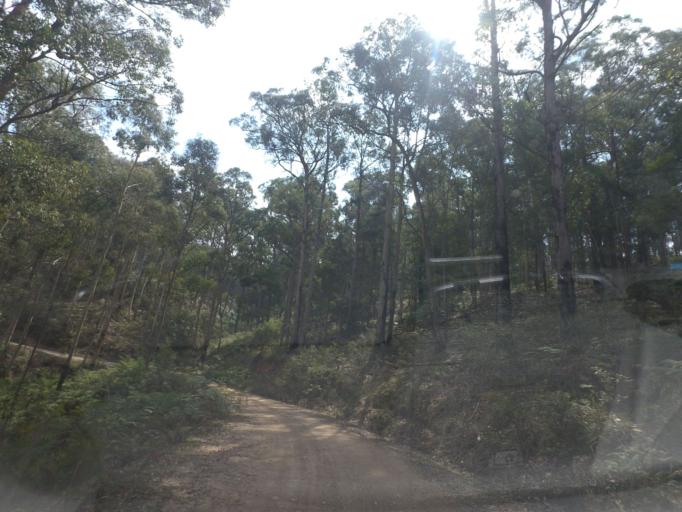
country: AU
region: Victoria
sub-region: Moorabool
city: Bacchus Marsh
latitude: -37.4613
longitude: 144.3792
